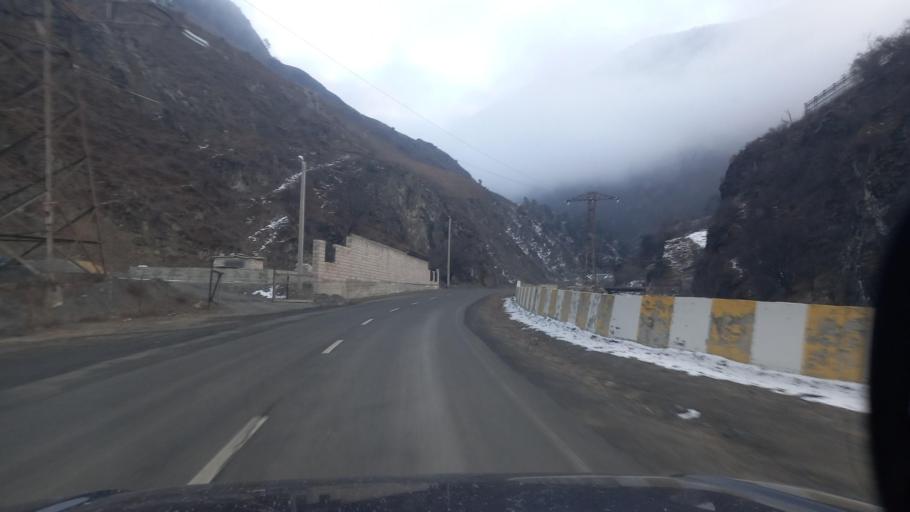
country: RU
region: Ingushetiya
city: Dzhayrakh
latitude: 42.7990
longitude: 44.7603
